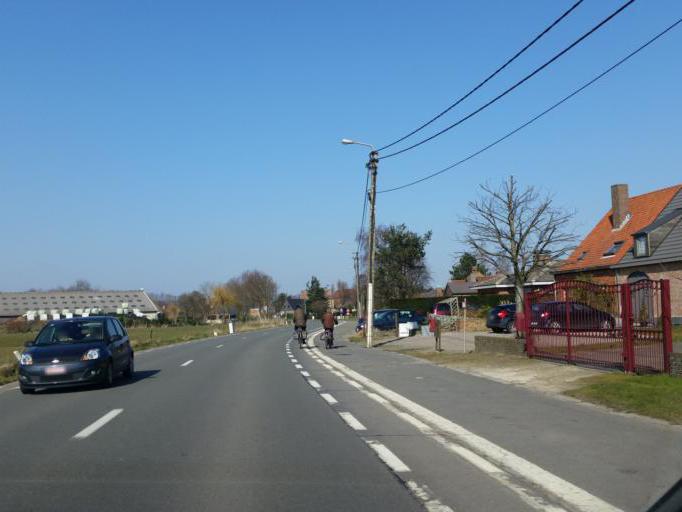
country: BE
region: Flanders
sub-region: Provincie Oost-Vlaanderen
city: Wachtebeke
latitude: 51.1625
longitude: 3.8612
